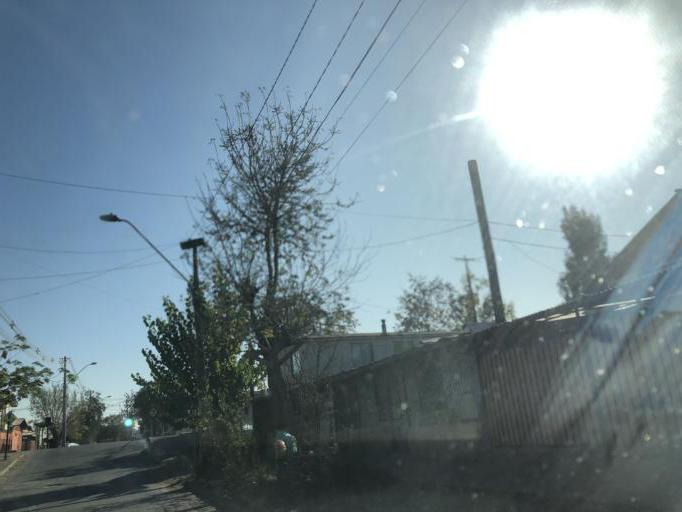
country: CL
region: Santiago Metropolitan
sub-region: Provincia de Cordillera
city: Puente Alto
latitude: -33.6172
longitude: -70.5935
